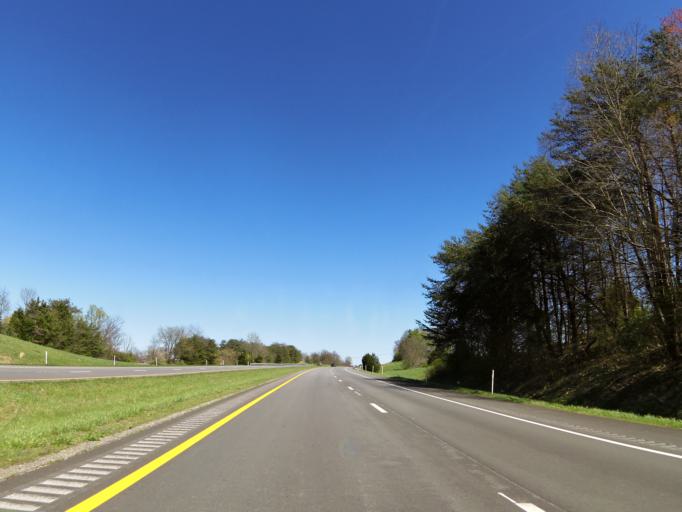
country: US
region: Kentucky
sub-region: Pulaski County
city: Somerset
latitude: 37.0984
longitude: -84.7690
